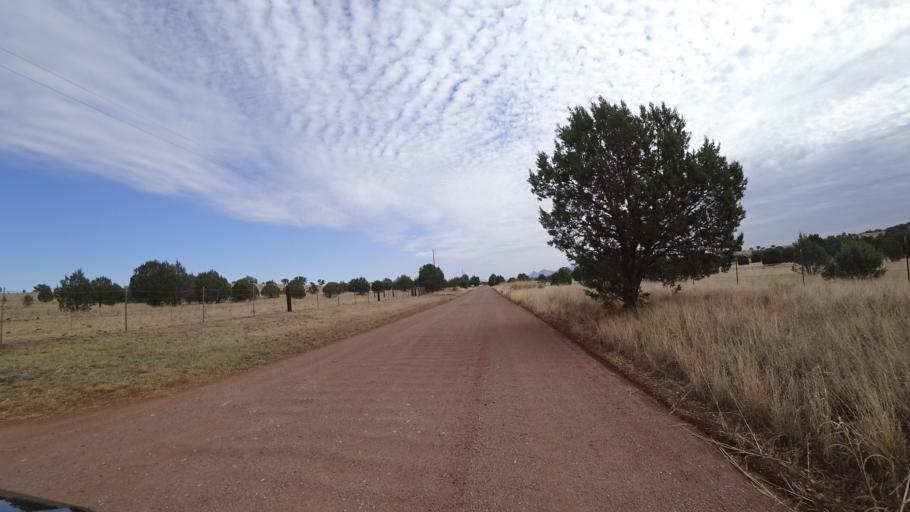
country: US
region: Arizona
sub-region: Cochise County
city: Huachuca City
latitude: 31.5399
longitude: -110.5298
